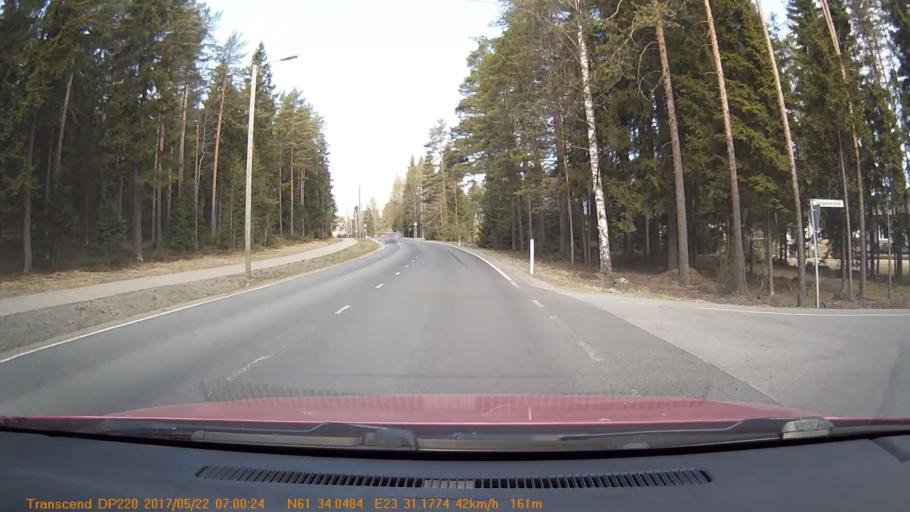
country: FI
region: Pirkanmaa
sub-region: Tampere
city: Yloejaervi
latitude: 61.5674
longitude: 23.5200
